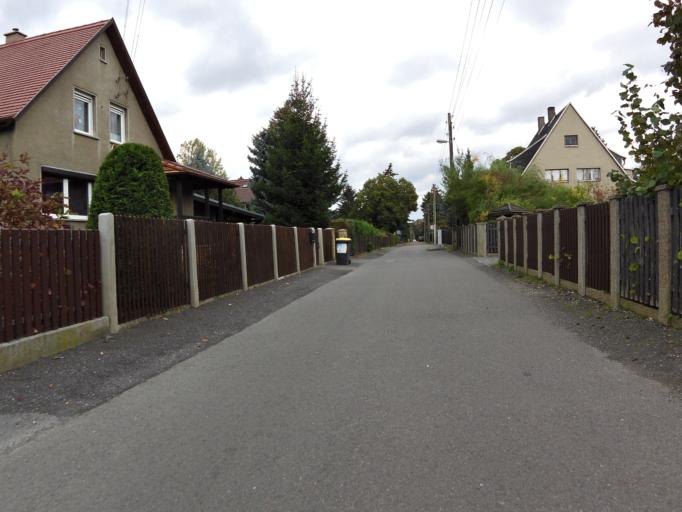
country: DE
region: Saxony
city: Grossposna
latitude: 51.3157
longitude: 12.4436
